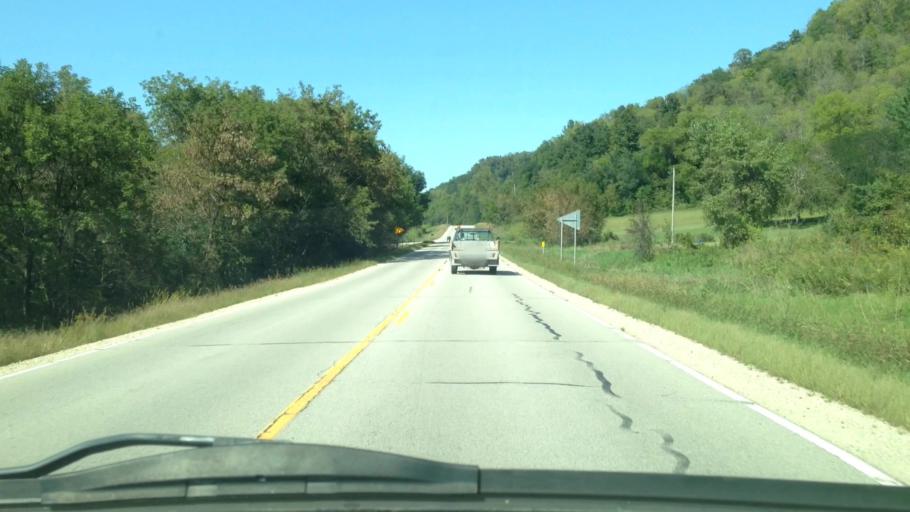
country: US
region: Minnesota
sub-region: Fillmore County
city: Rushford
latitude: 43.7715
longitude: -91.7638
